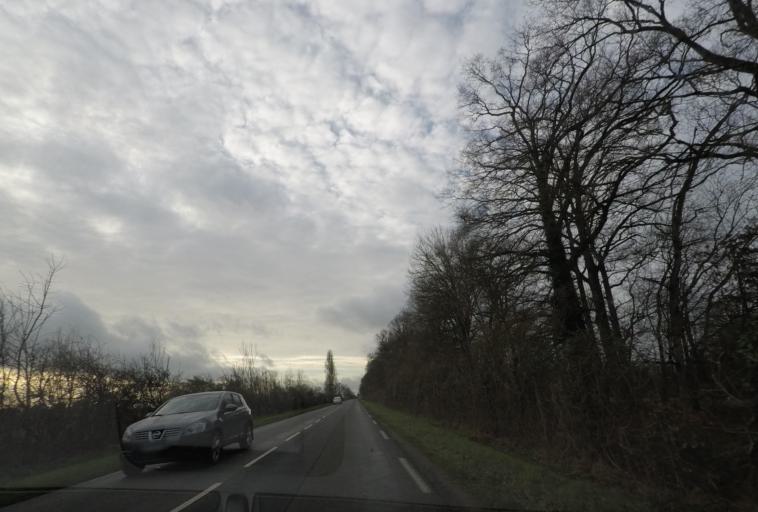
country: FR
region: Pays de la Loire
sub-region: Departement de la Sarthe
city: Saint-Calais
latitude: 47.9472
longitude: 0.7527
